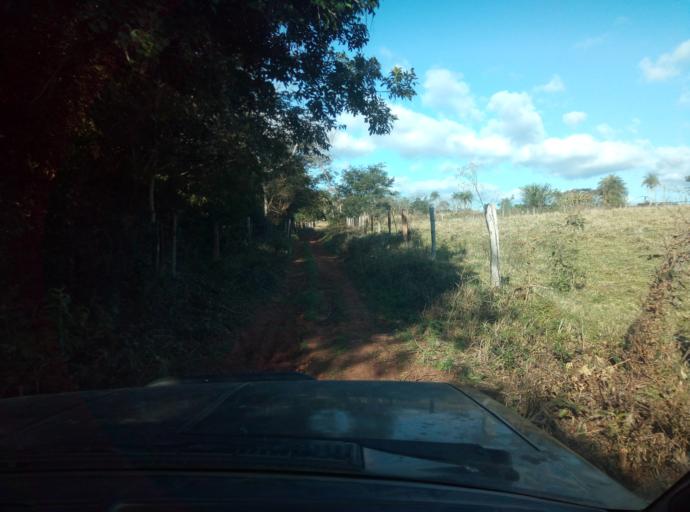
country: PY
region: Caaguazu
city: Carayao
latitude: -25.1746
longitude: -56.2711
